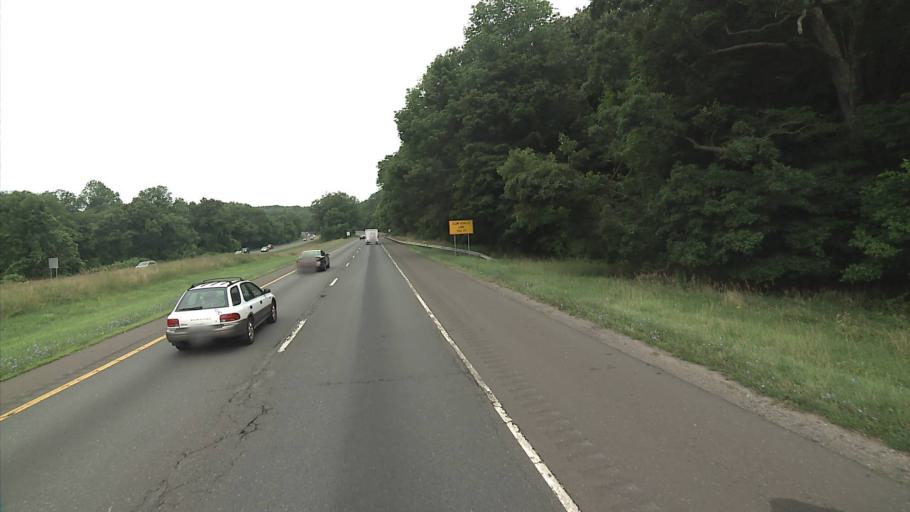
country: US
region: Connecticut
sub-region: Fairfield County
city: Newtown
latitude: 41.4275
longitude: -73.3087
